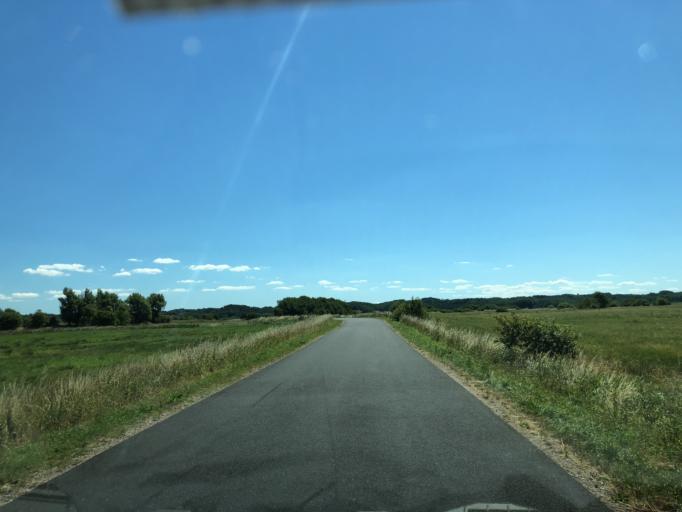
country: DK
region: Central Jutland
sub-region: Viborg Kommune
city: Viborg
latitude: 56.5521
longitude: 9.4285
